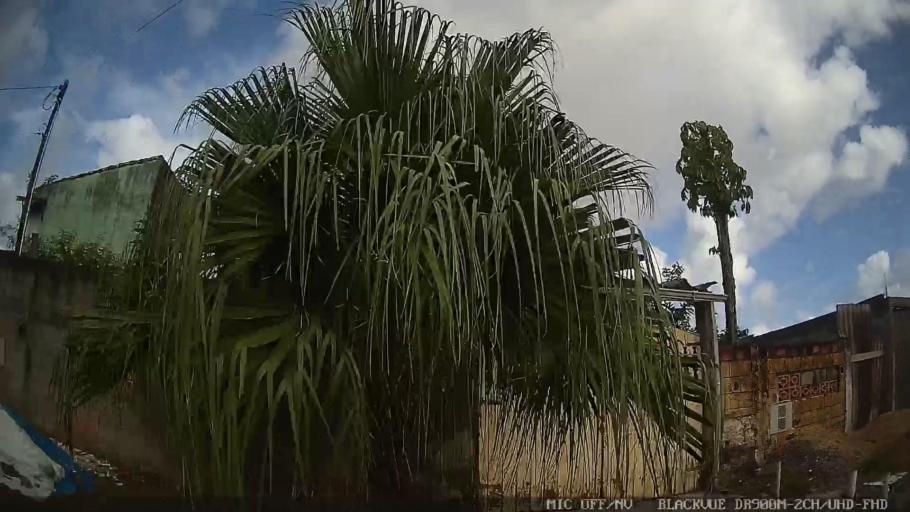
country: BR
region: Sao Paulo
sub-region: Itanhaem
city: Itanhaem
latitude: -24.1947
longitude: -46.8204
